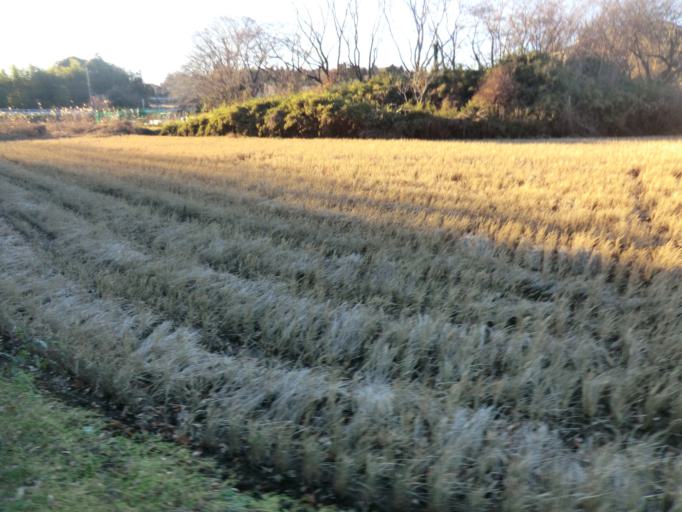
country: JP
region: Ibaraki
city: Mitsukaido
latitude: 36.0447
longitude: 139.9751
